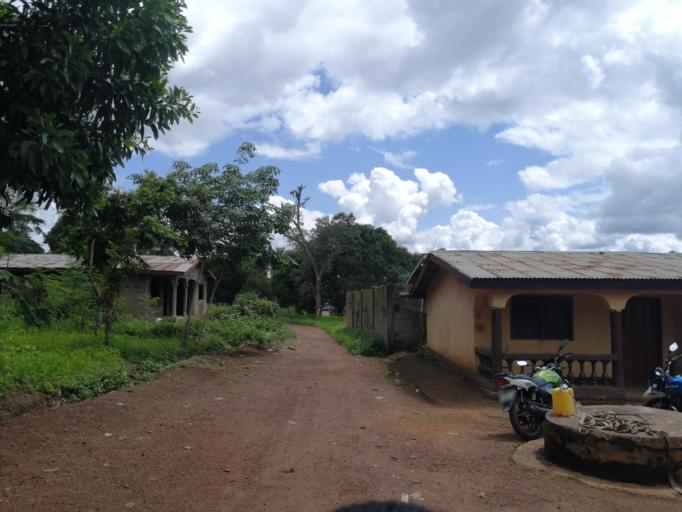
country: SL
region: Northern Province
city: Port Loko
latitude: 8.7724
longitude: -12.7777
